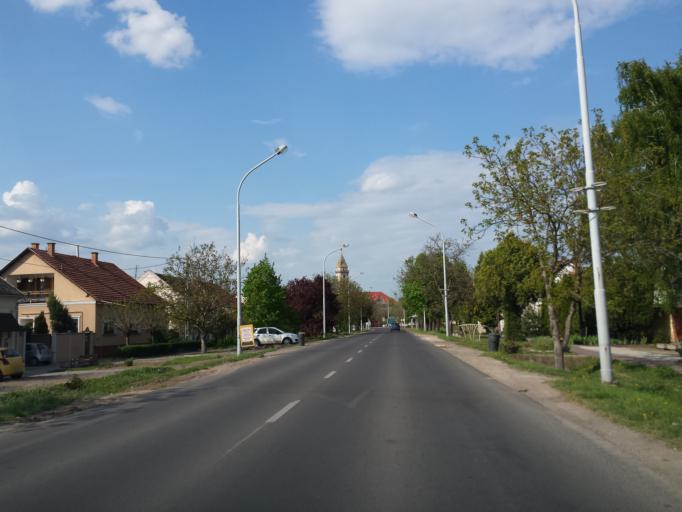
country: HU
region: Csongrad
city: Mako
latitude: 46.2256
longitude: 20.4801
